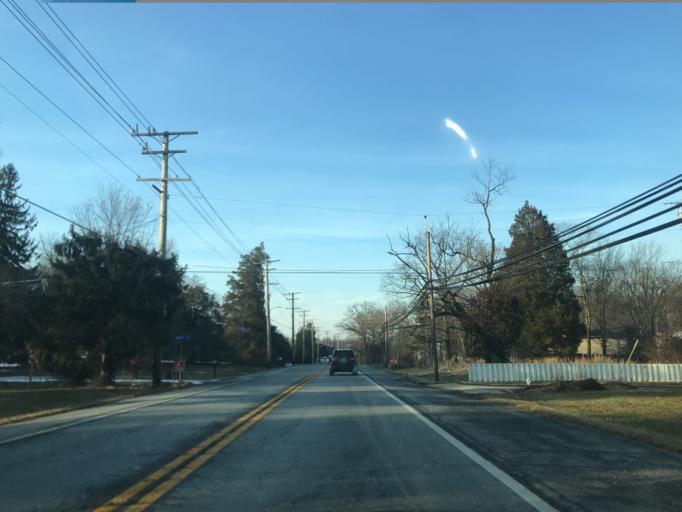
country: US
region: Maryland
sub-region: Harford County
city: Edgewood
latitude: 39.4166
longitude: -76.3278
